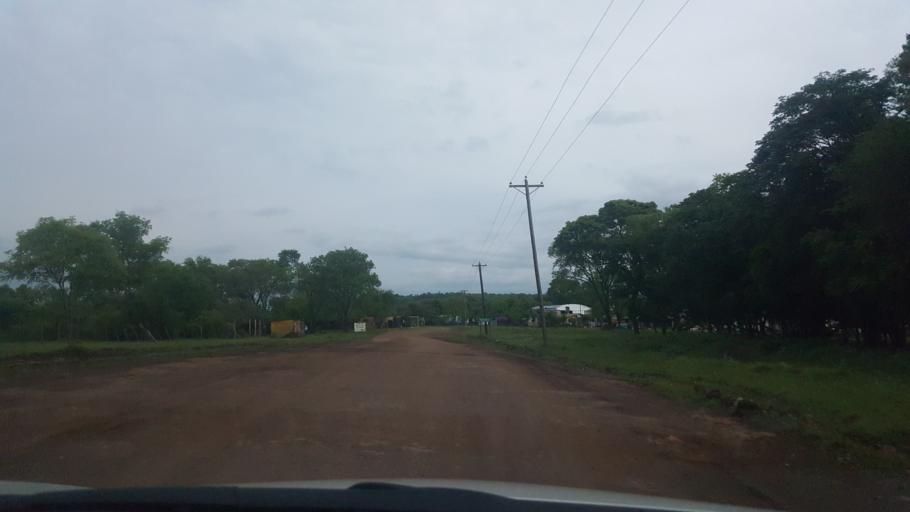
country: AR
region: Misiones
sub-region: Departamento de Candelaria
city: Candelaria
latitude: -27.5573
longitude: -55.7059
